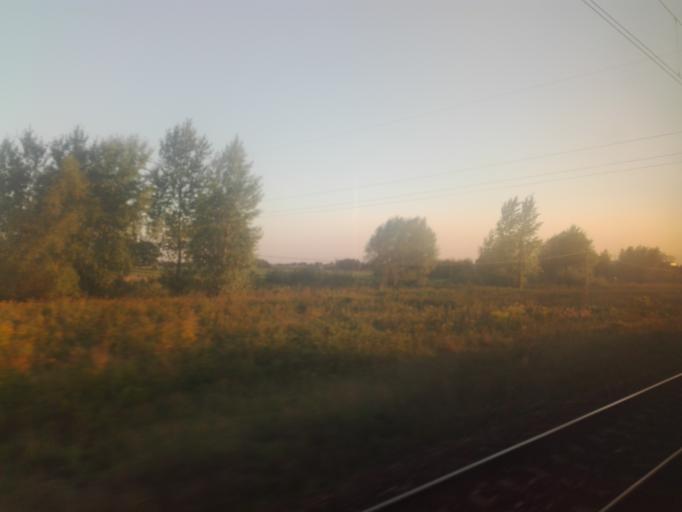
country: PL
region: Masovian Voivodeship
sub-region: Powiat warszawski zachodni
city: Bieniewice
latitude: 52.1863
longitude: 20.5861
